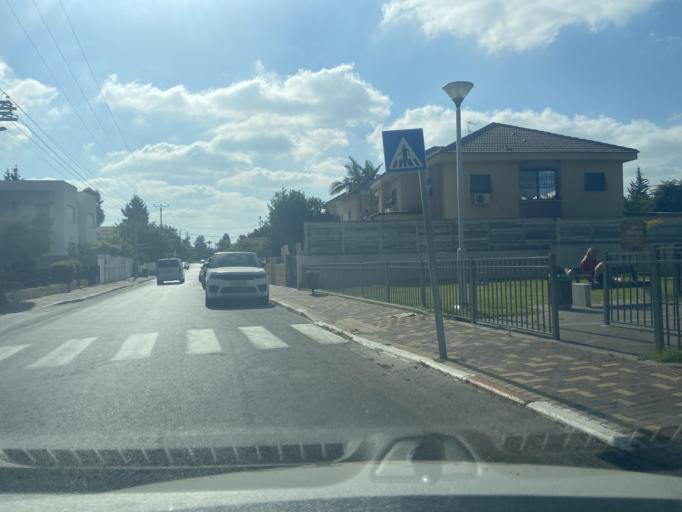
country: IL
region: Central District
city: Yehud
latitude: 32.0344
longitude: 34.8953
